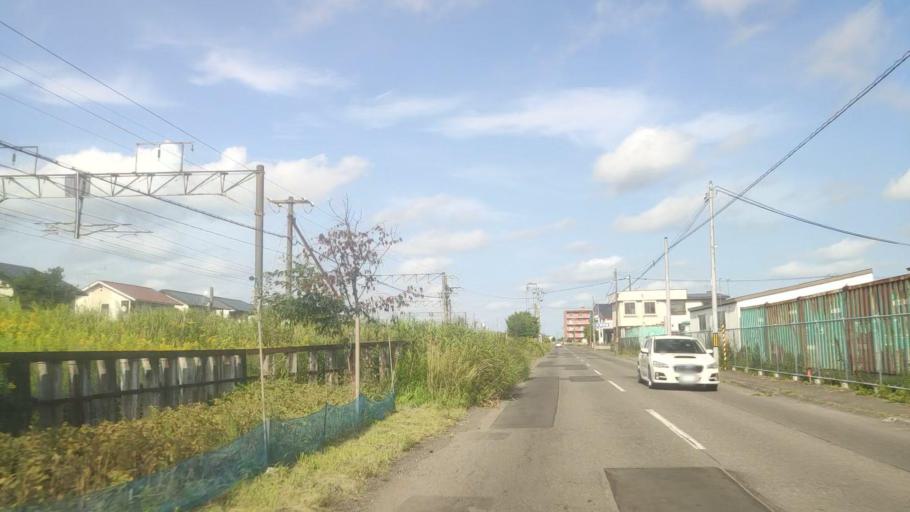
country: JP
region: Hokkaido
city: Tomakomai
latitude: 42.6475
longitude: 141.6207
